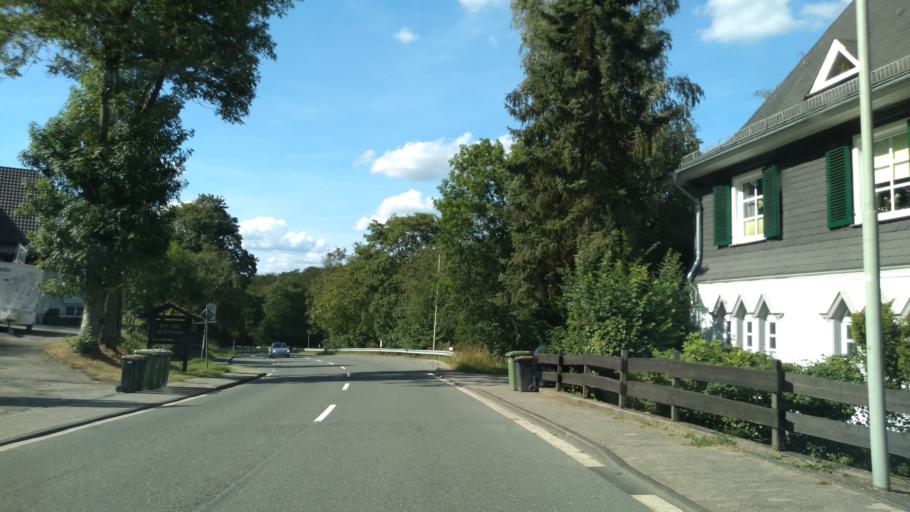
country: DE
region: North Rhine-Westphalia
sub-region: Regierungsbezirk Arnsberg
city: Olpe
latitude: 51.0525
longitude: 7.8585
